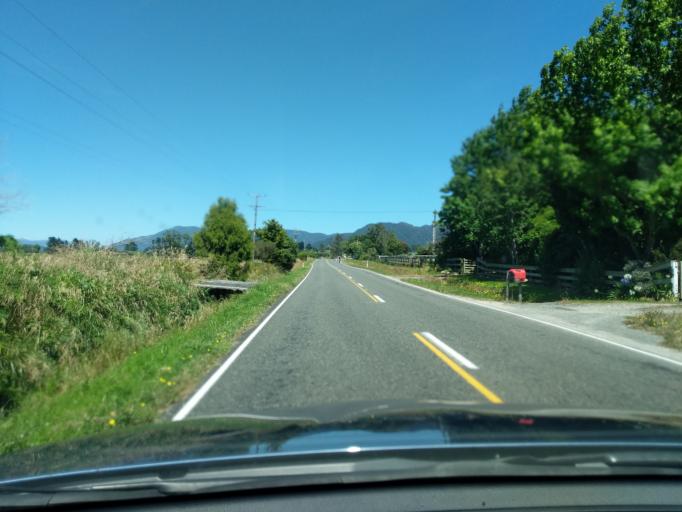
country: NZ
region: Tasman
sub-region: Tasman District
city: Takaka
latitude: -40.6848
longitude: 172.6578
